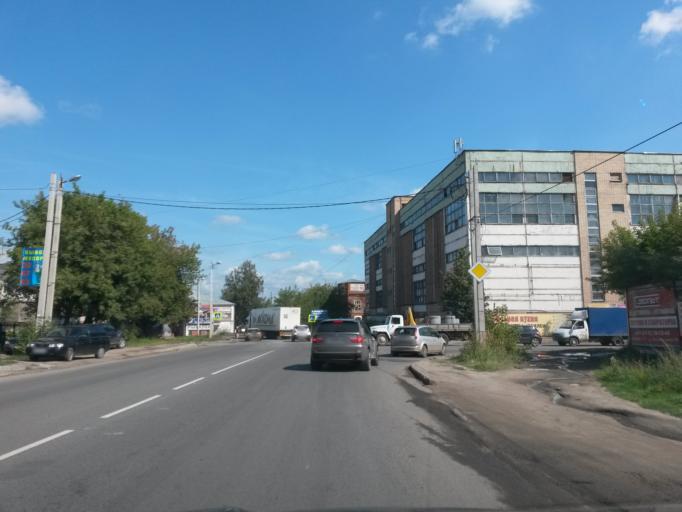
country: RU
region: Ivanovo
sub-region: Gorod Ivanovo
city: Ivanovo
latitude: 57.0096
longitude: 40.9529
